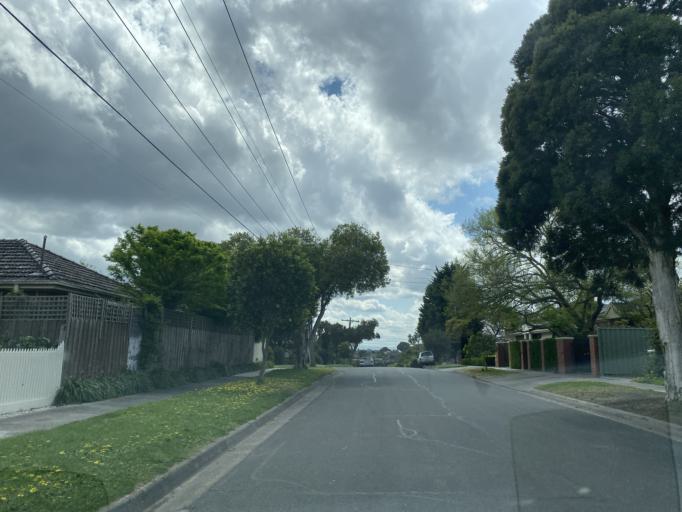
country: AU
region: Victoria
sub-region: Whitehorse
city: Burwood
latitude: -37.8586
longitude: 145.1284
